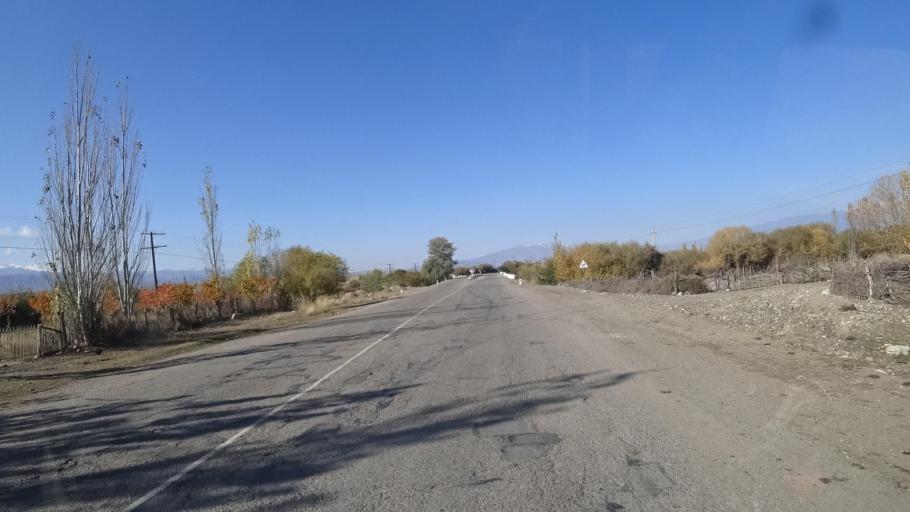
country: KG
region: Ysyk-Koel
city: Balykchy
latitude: 42.3180
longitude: 76.3969
